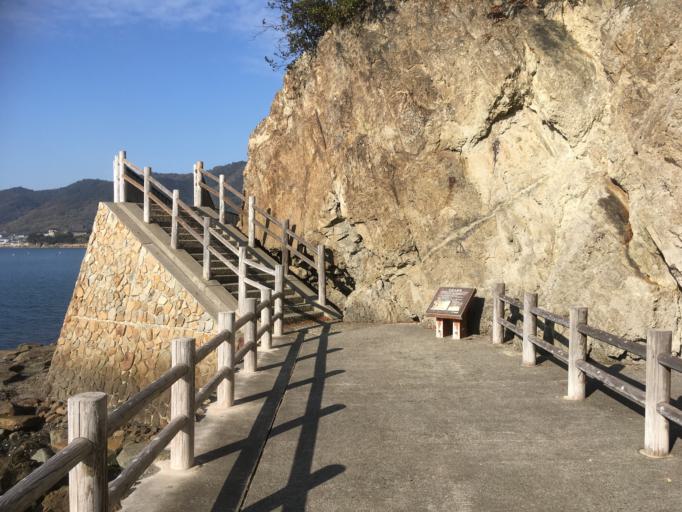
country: JP
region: Hiroshima
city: Fukuyama
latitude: 34.3824
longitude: 133.3925
